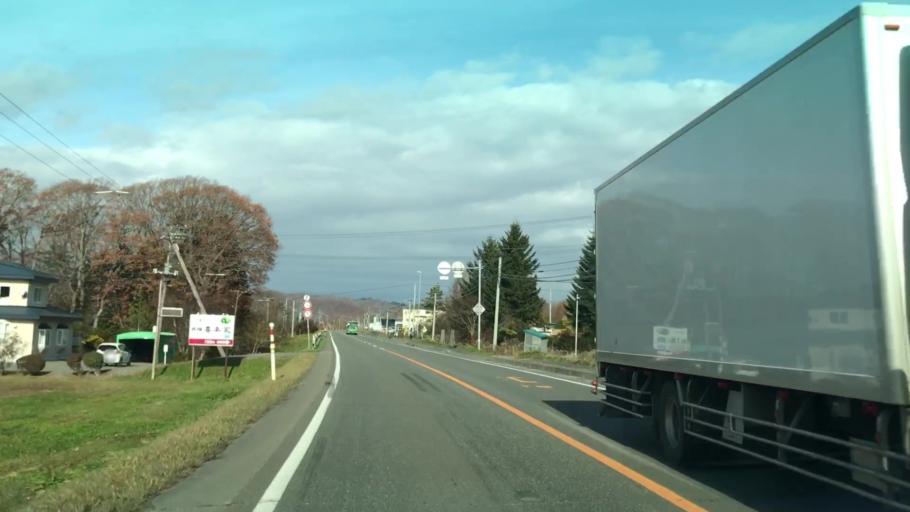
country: JP
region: Hokkaido
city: Shizunai-furukawacho
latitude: 42.6003
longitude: 142.1492
